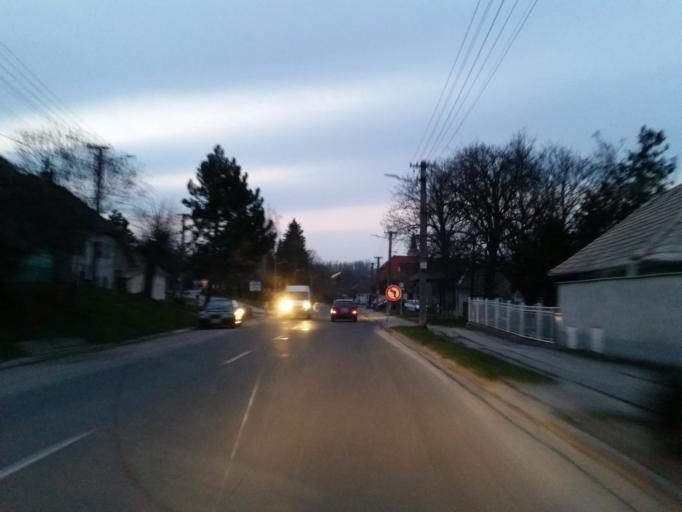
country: SK
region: Trnavsky
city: Vrbove
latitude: 48.6260
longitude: 17.7205
